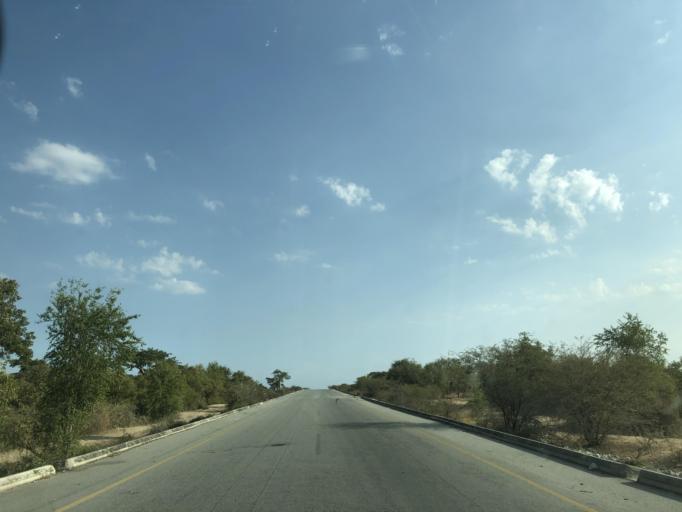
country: AO
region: Benguela
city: Benguela
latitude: -13.2043
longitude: 13.7636
